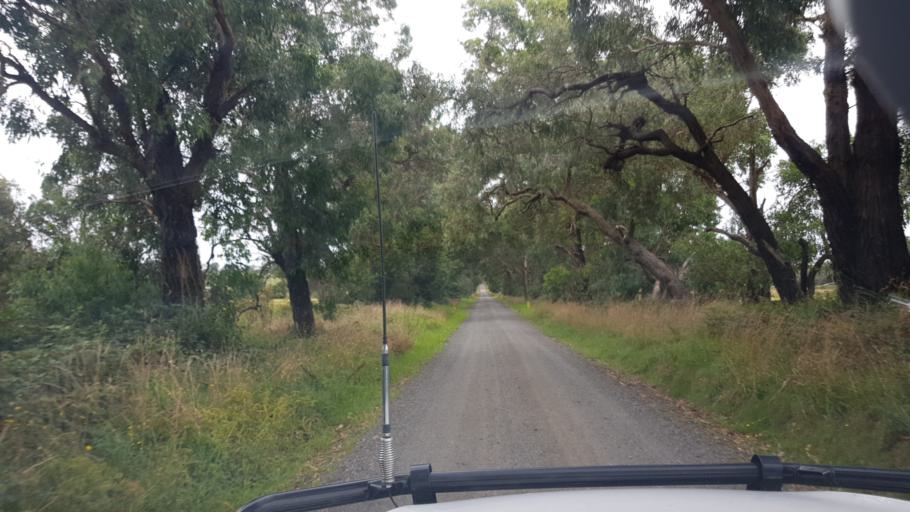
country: AU
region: Victoria
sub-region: Baw Baw
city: Warragul
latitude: -38.1848
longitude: 145.8258
